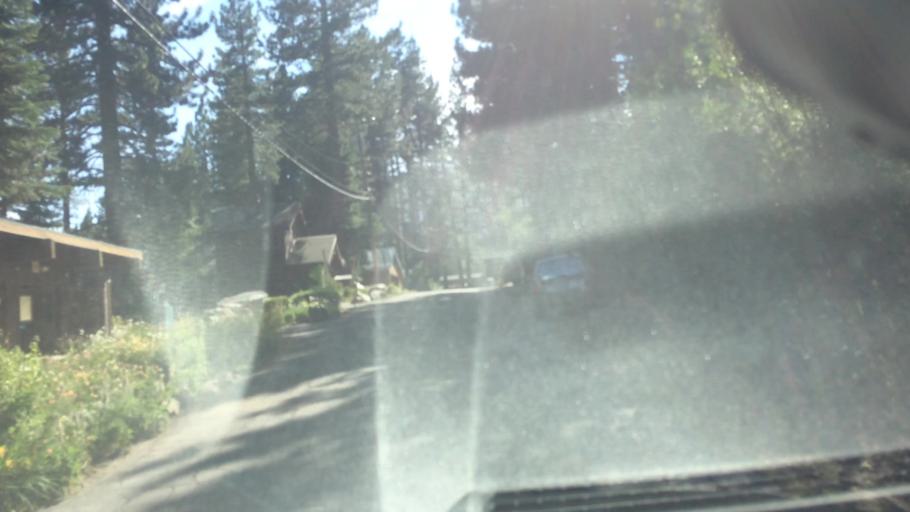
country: US
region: California
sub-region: Placer County
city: Sunnyside-Tahoe City
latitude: 39.2026
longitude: -120.2268
